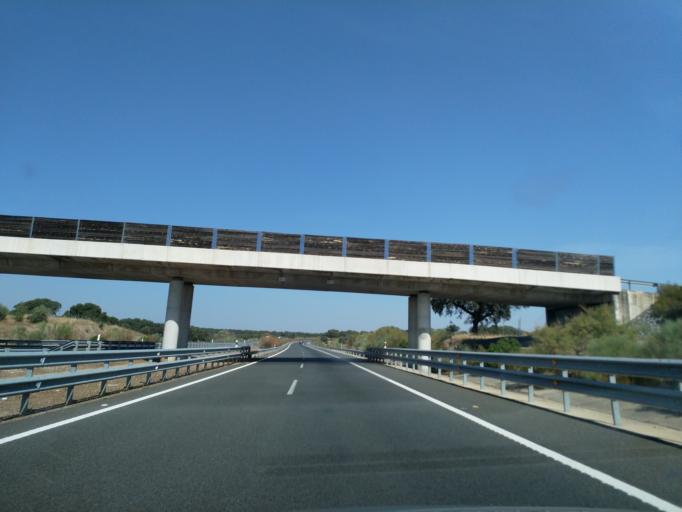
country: ES
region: Extremadura
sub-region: Provincia de Badajoz
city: Mirandilla
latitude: 38.9954
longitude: -6.3297
